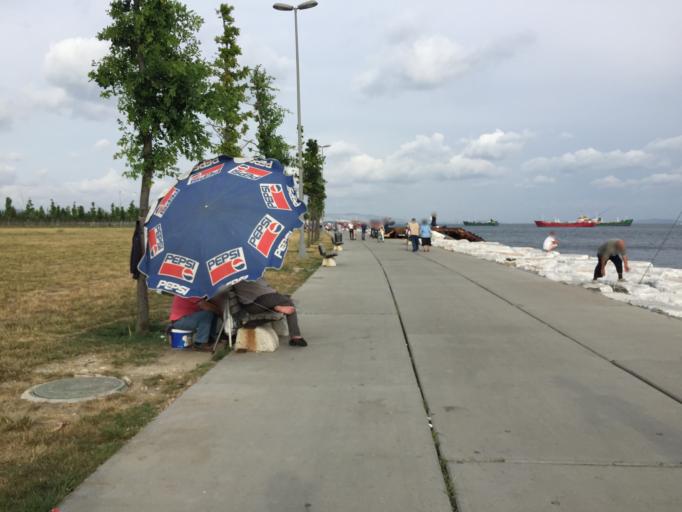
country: TR
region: Istanbul
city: Istanbul
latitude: 40.9967
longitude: 28.9431
